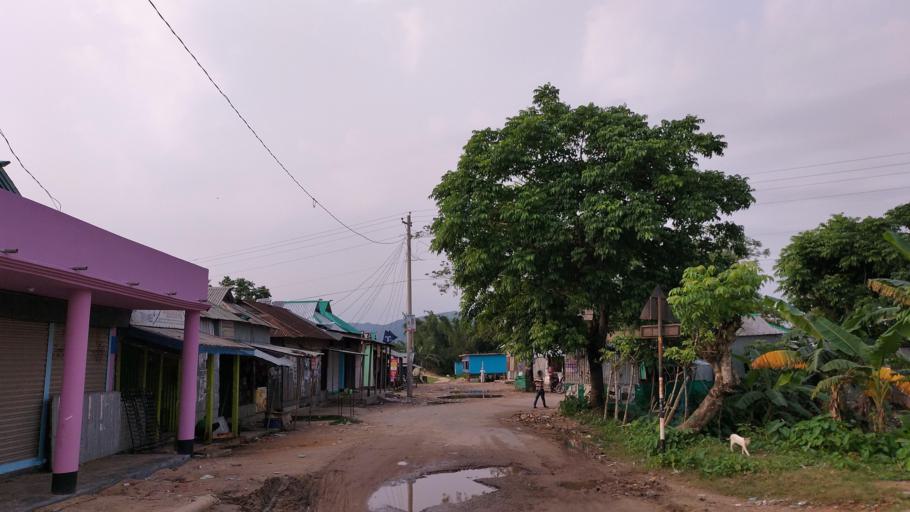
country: BD
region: Dhaka
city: Netrakona
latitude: 25.1342
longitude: 90.9137
